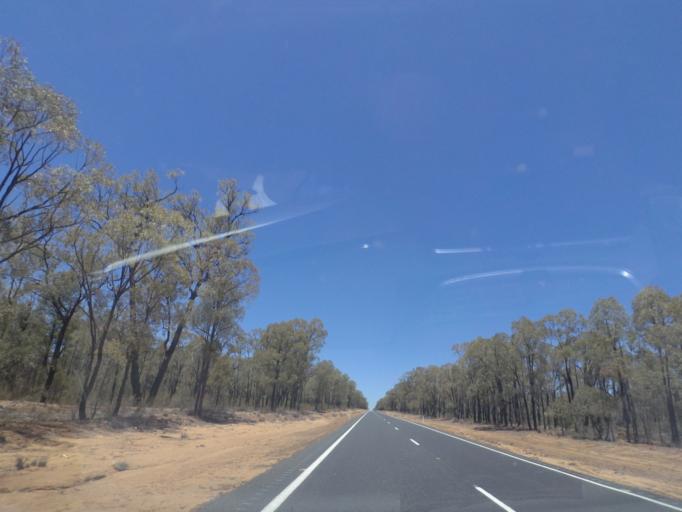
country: AU
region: New South Wales
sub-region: Narrabri
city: Narrabri
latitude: -30.7287
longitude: 149.5216
